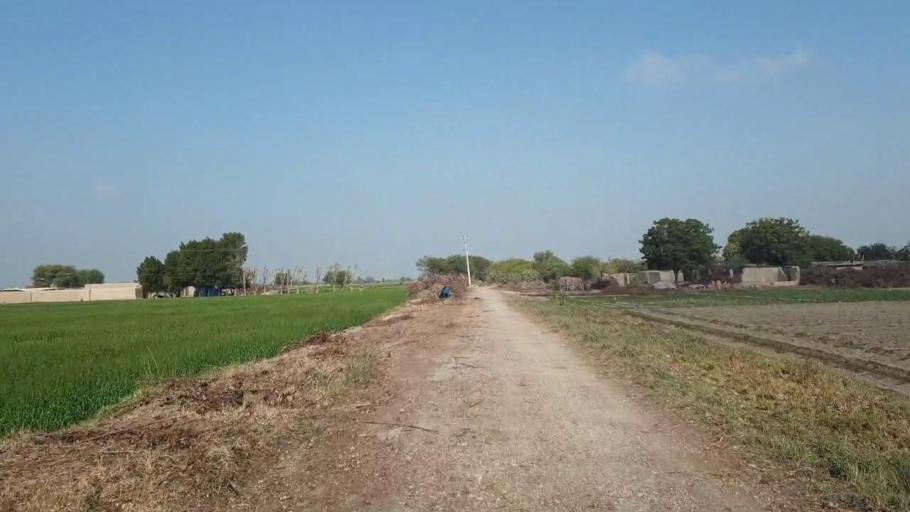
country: PK
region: Sindh
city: Shahdadpur
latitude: 26.0249
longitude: 68.6110
